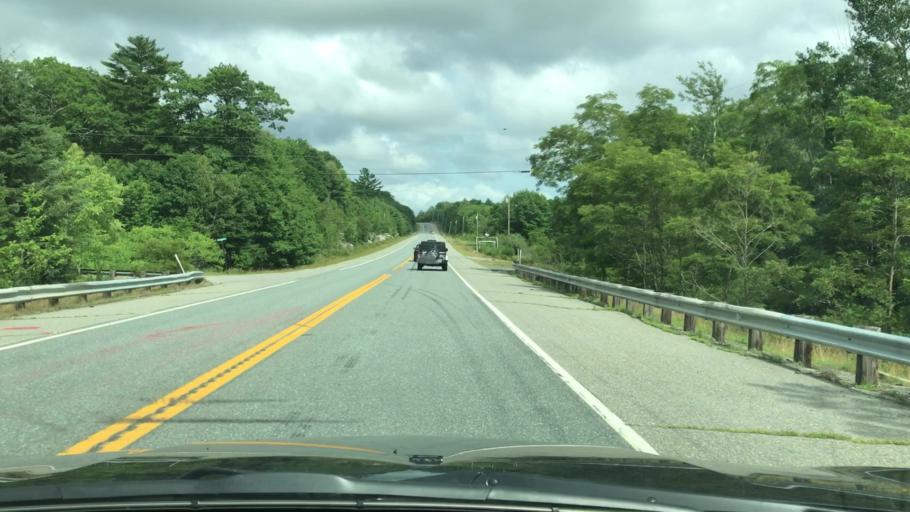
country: US
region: Maine
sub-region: Hancock County
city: Orland
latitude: 44.5660
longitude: -68.6115
